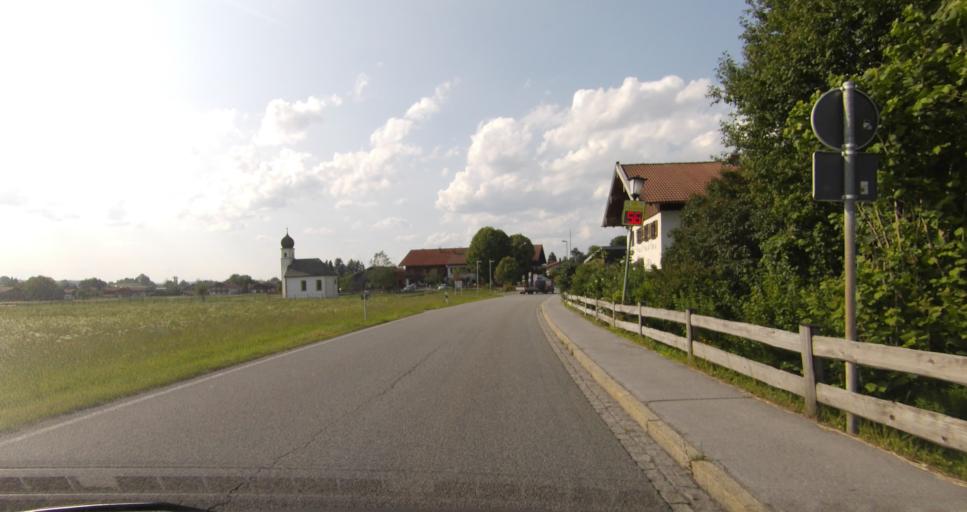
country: DE
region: Bavaria
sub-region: Upper Bavaria
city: Fischbachau
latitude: 47.7550
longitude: 11.9442
